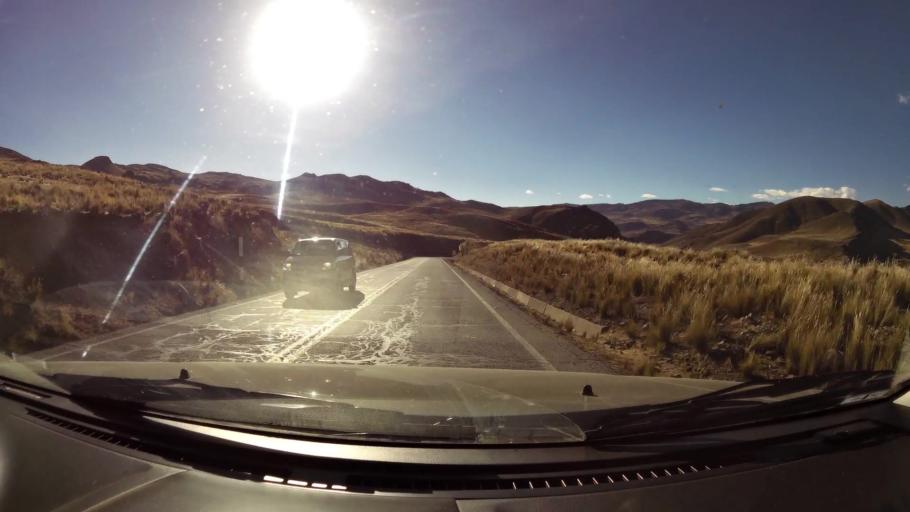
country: PE
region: Huancavelica
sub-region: Huaytara
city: Pilpichaca
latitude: -13.3630
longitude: -74.9539
